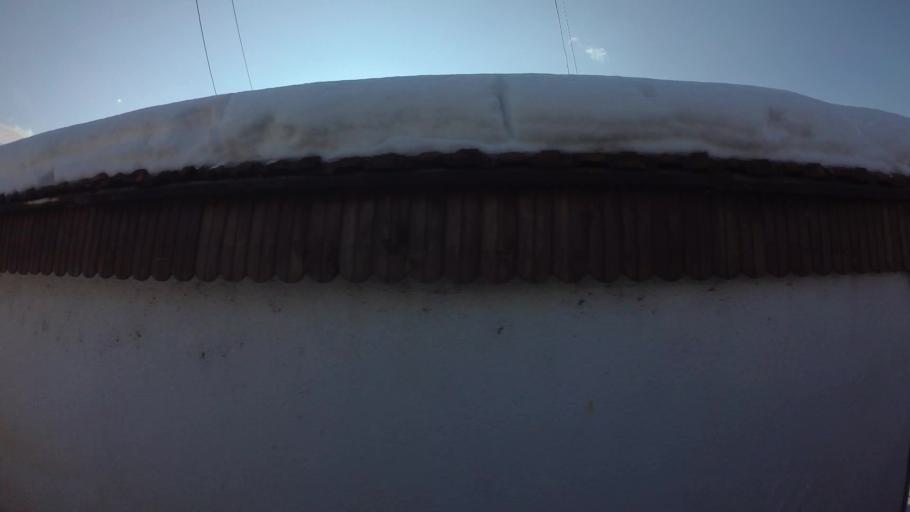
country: BA
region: Federation of Bosnia and Herzegovina
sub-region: Kanton Sarajevo
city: Sarajevo
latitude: 43.8202
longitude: 18.3190
